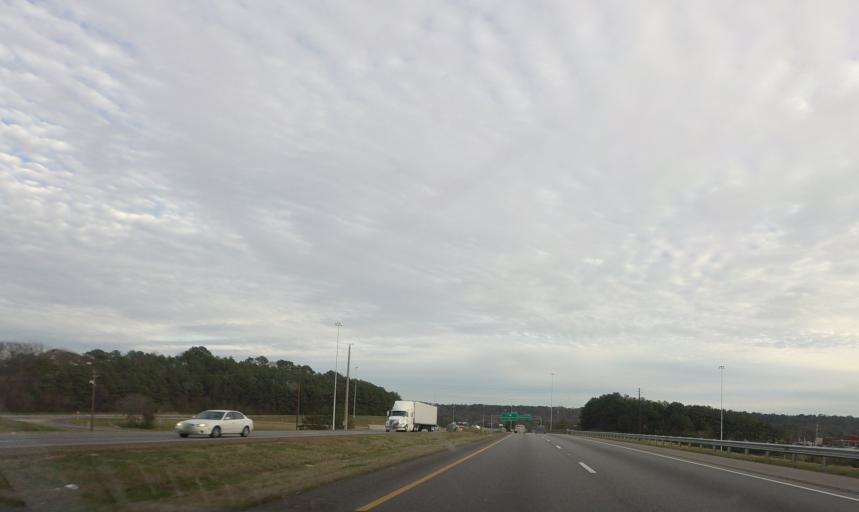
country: US
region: Alabama
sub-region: Jefferson County
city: Irondale
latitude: 33.5349
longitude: -86.7220
